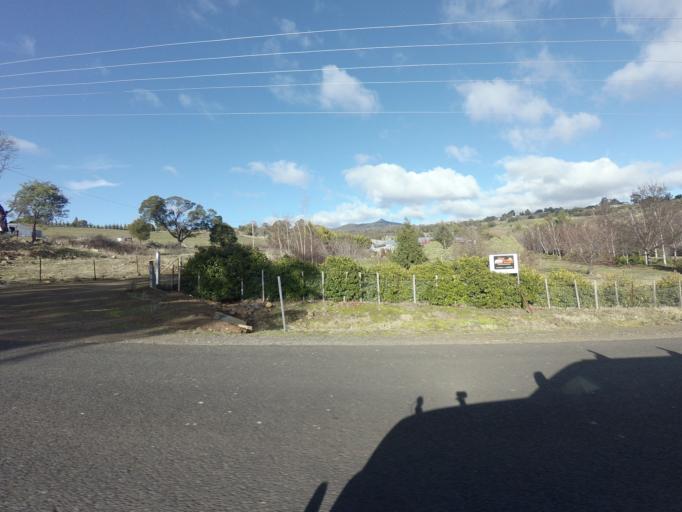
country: AU
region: Tasmania
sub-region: Derwent Valley
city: New Norfolk
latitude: -42.7969
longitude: 147.1271
